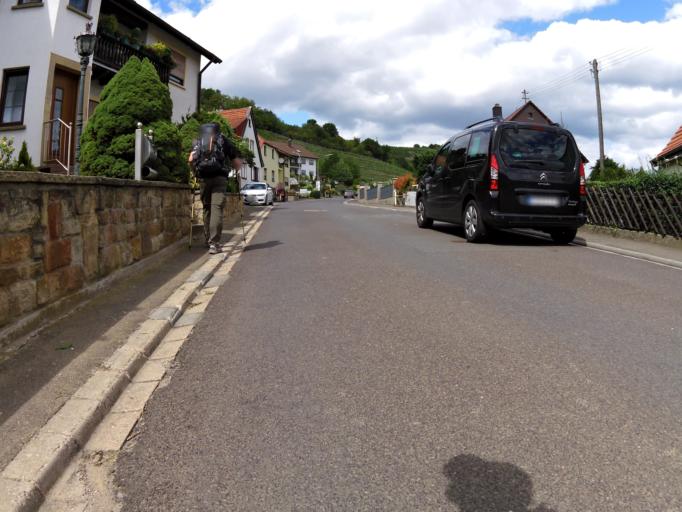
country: DE
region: Rheinland-Pfalz
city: Niederhausen
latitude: 49.8046
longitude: 7.7805
